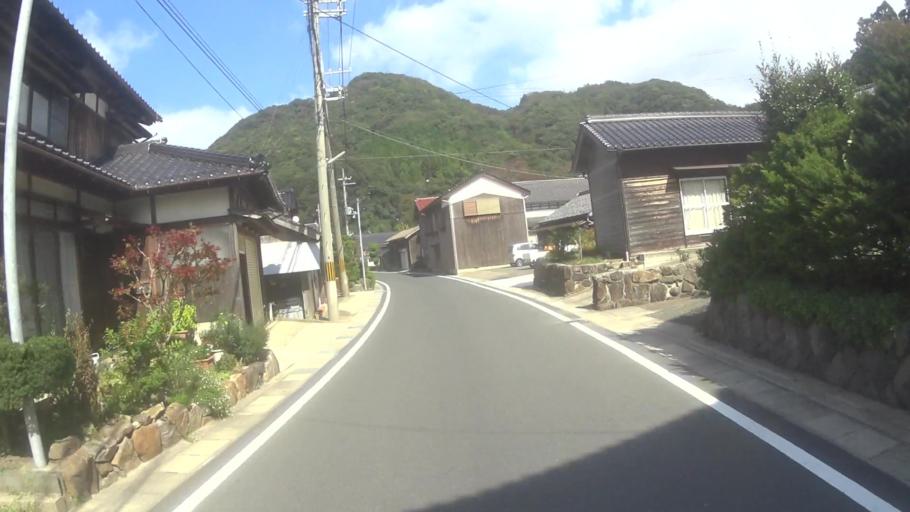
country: JP
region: Kyoto
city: Miyazu
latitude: 35.7355
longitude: 135.1101
